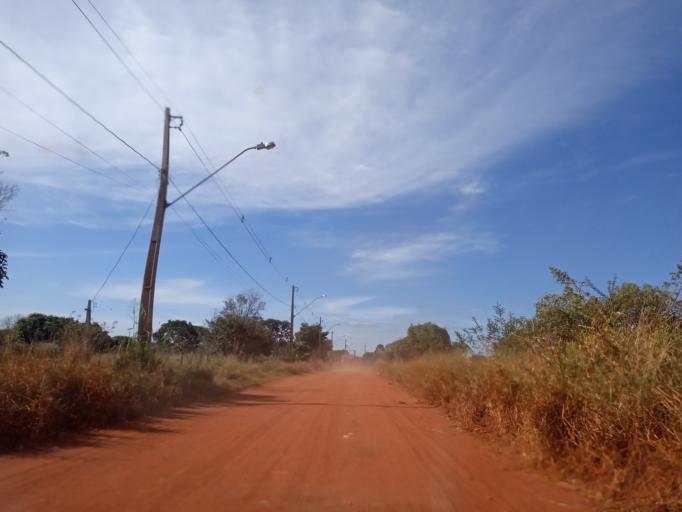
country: BR
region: Minas Gerais
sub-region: Ituiutaba
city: Ituiutaba
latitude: -18.9575
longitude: -49.4888
